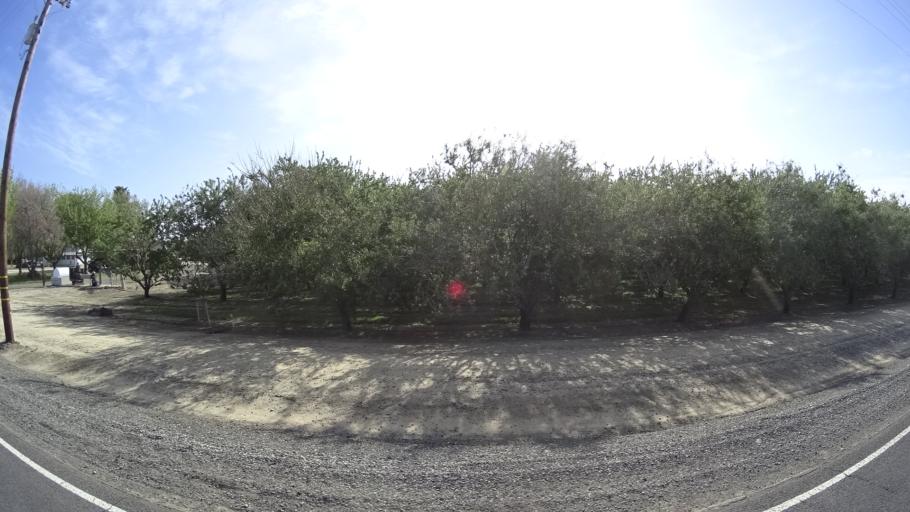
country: US
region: California
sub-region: Glenn County
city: Hamilton City
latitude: 39.6124
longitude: -122.0075
